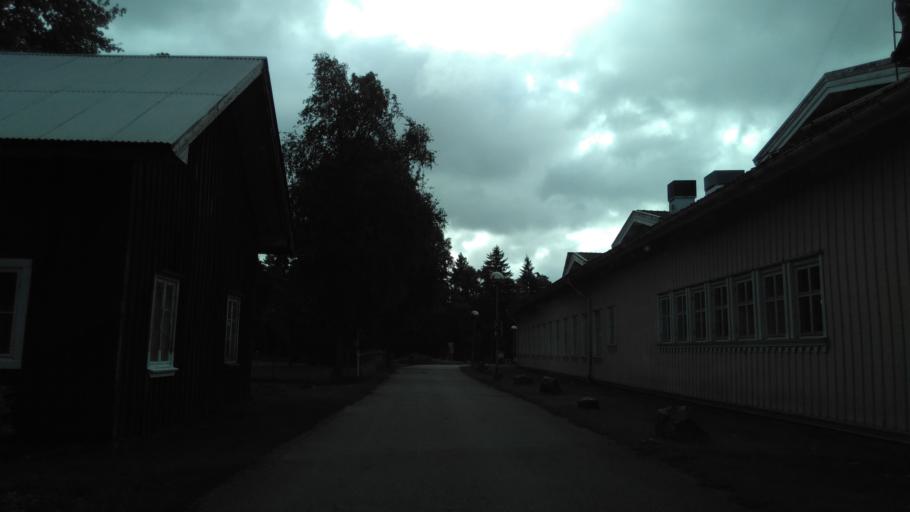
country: SE
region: Vaestra Goetaland
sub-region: Marks Kommun
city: Fritsla
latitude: 57.5901
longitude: 12.7506
